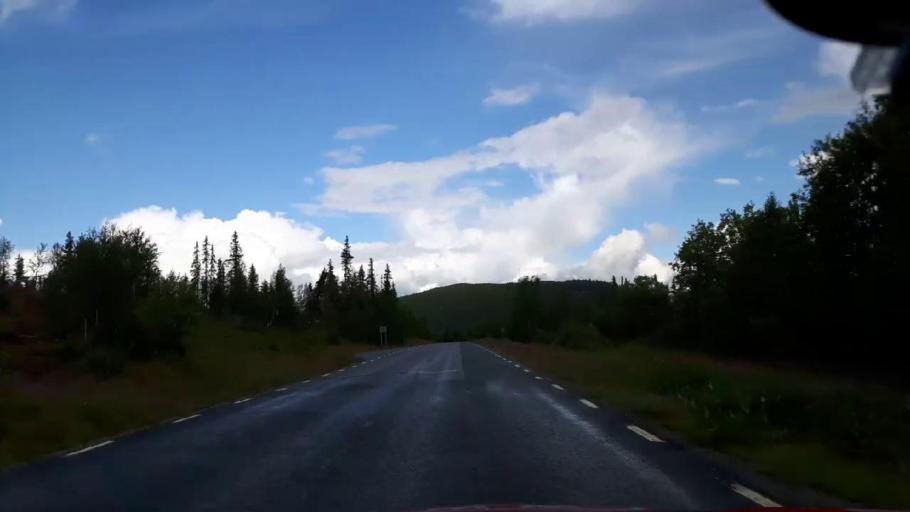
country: SE
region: Vaesterbotten
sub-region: Vilhelmina Kommun
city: Sjoberg
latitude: 65.0151
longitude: 15.1707
